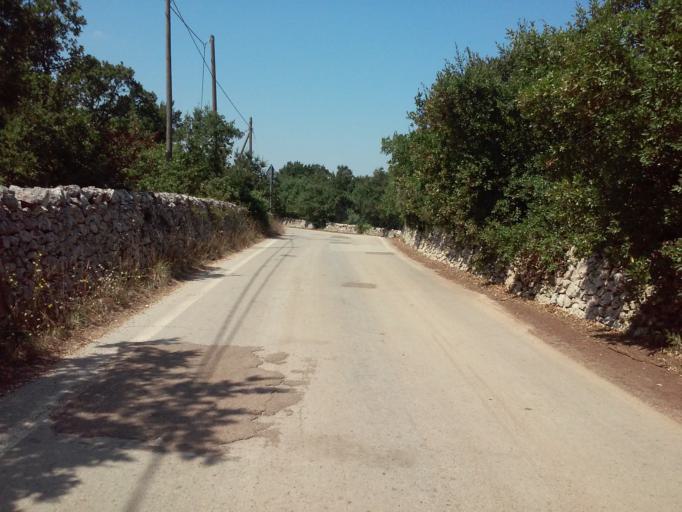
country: IT
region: Apulia
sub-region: Provincia di Bari
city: Alberobello
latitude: 40.8039
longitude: 17.2080
